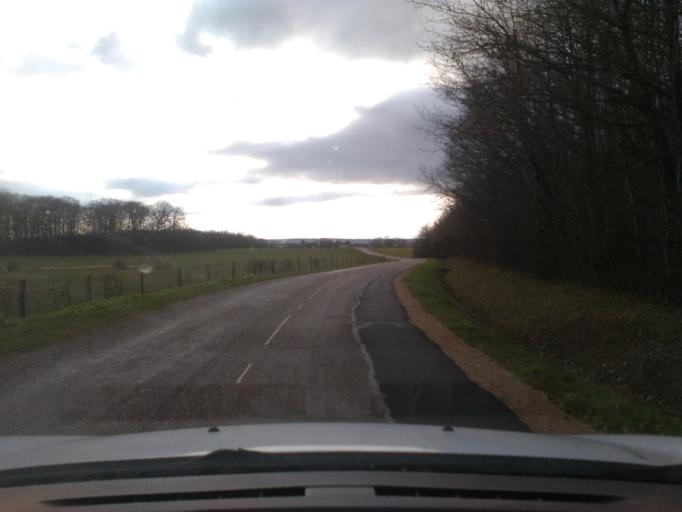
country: FR
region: Lorraine
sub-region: Departement des Vosges
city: Vittel
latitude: 48.3332
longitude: 5.9890
